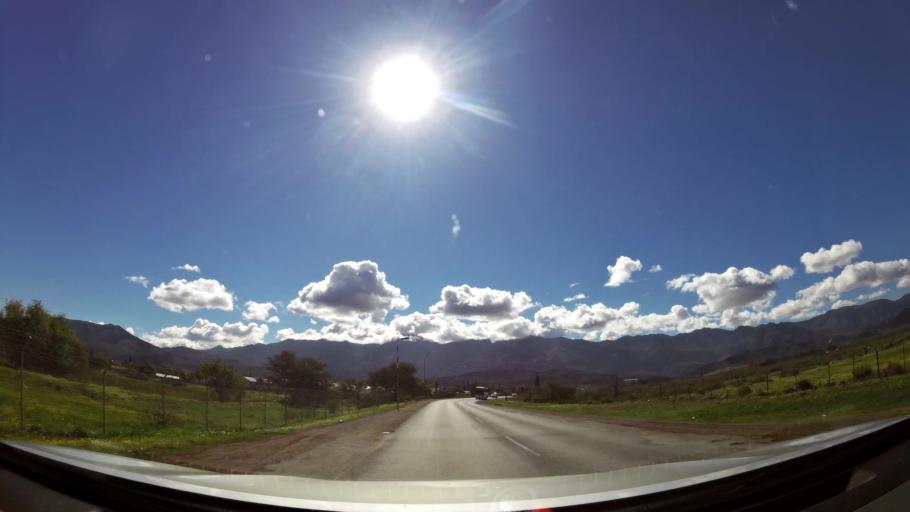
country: ZA
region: Western Cape
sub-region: Cape Winelands District Municipality
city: Ashton
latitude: -33.8127
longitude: 19.8975
